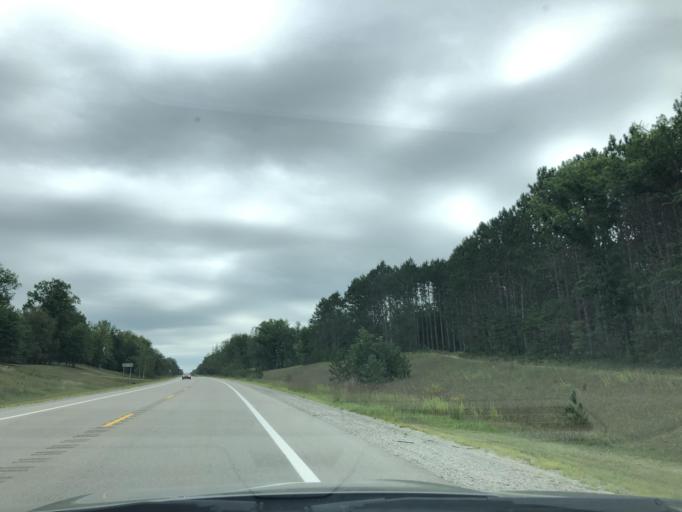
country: US
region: Michigan
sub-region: Clare County
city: Harrison
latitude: 44.0314
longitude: -85.0158
